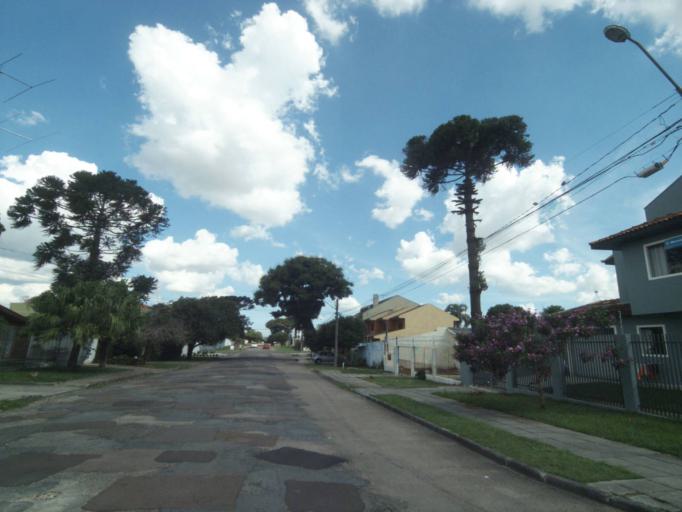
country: BR
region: Parana
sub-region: Pinhais
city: Pinhais
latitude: -25.4525
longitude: -49.2110
